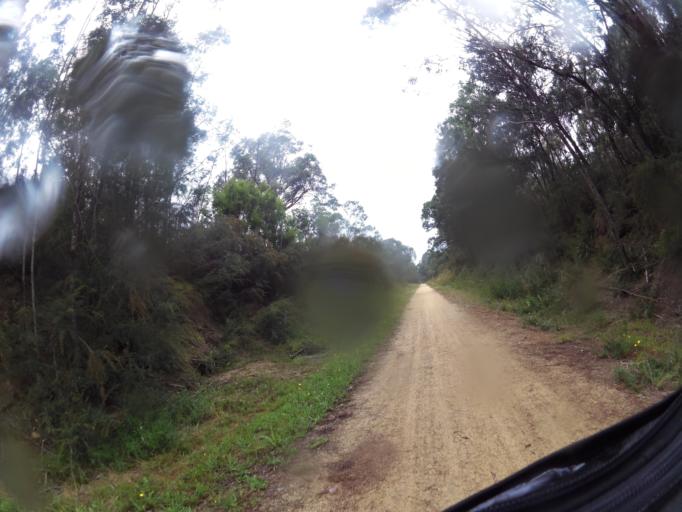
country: AU
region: Victoria
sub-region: East Gippsland
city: Bairnsdale
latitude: -37.7463
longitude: 147.8105
